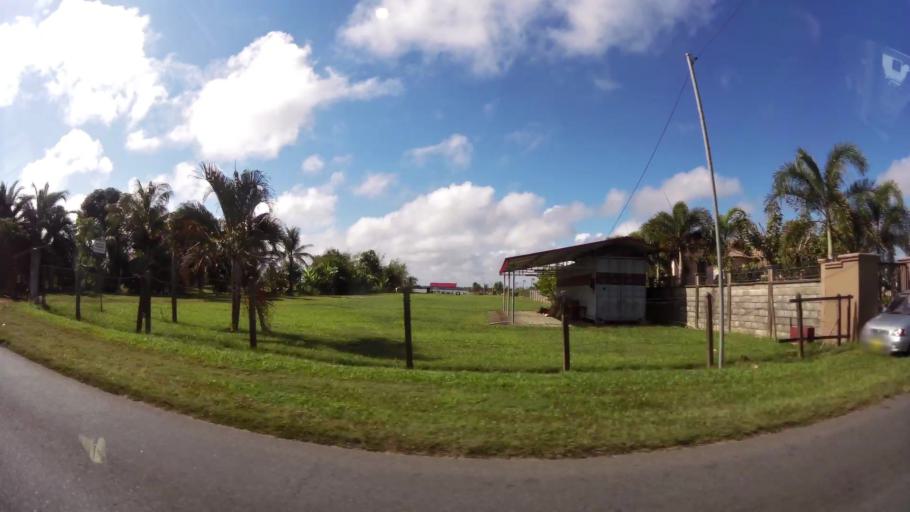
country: SR
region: Paramaribo
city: Paramaribo
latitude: 5.8361
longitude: -55.1263
